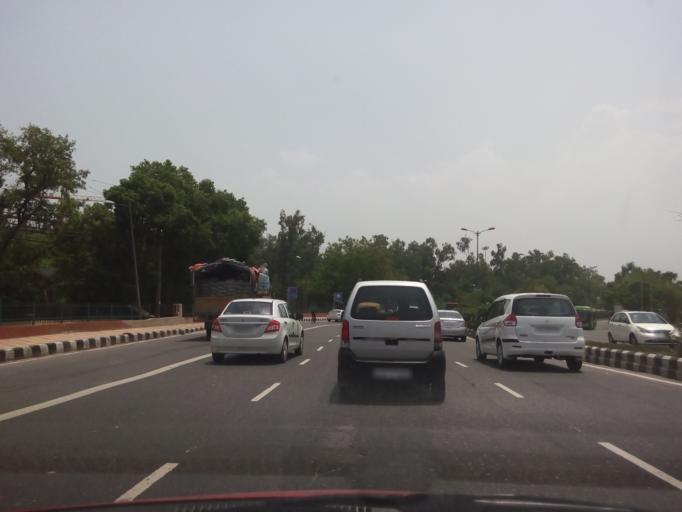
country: IN
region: NCT
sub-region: North West Delhi
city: Pitampura
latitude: 28.6601
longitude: 77.1293
